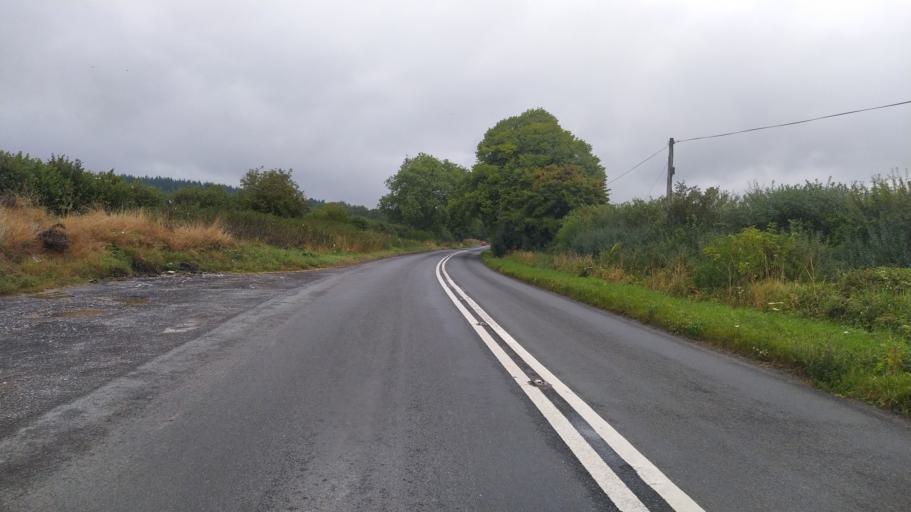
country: GB
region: England
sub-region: Wiltshire
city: Ansty
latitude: 51.0177
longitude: -2.0939
